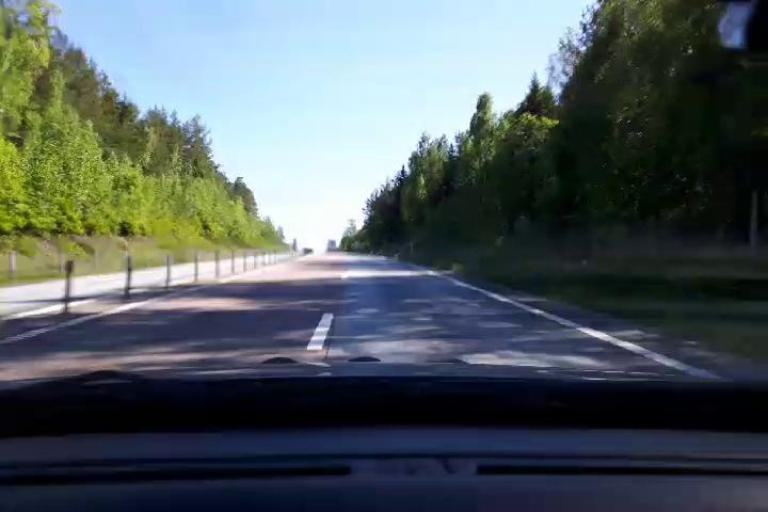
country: SE
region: Gaevleborg
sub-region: Soderhamns Kommun
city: Soderhamn
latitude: 61.2699
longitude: 17.0271
